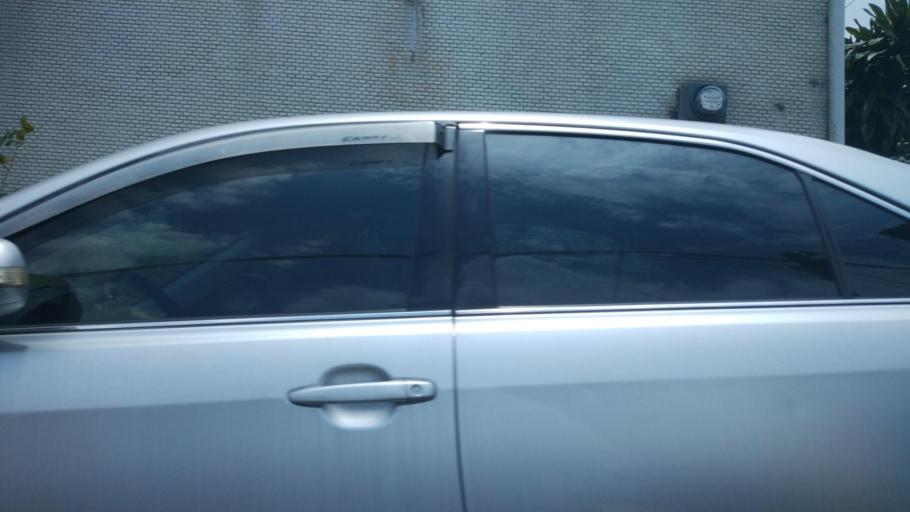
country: TW
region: Taipei
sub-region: Taipei
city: Banqiao
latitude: 24.9467
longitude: 121.4877
